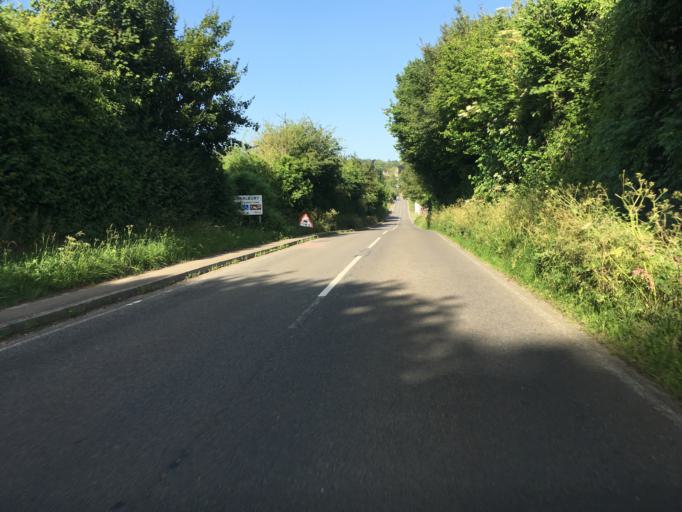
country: GB
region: England
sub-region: Oxfordshire
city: Charlbury
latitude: 51.8728
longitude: -1.4940
